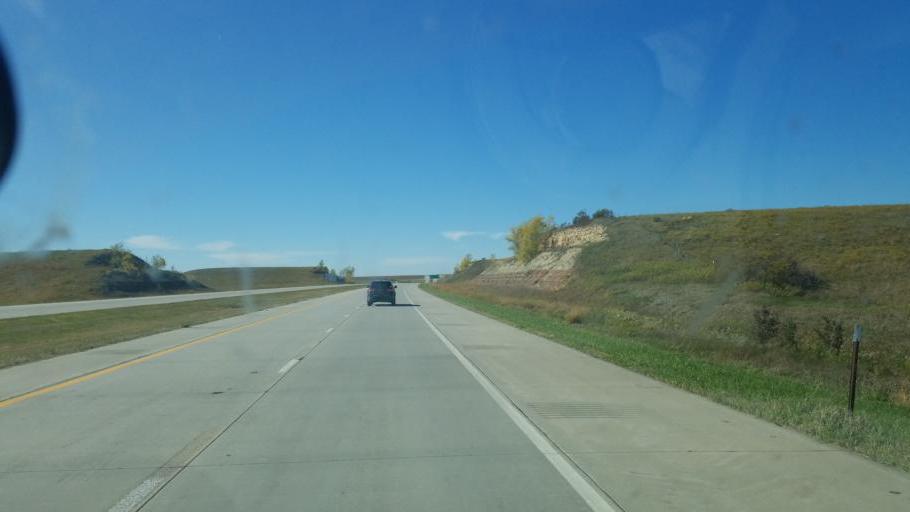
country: US
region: Kansas
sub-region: Riley County
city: Manhattan
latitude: 39.0630
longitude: -96.5493
